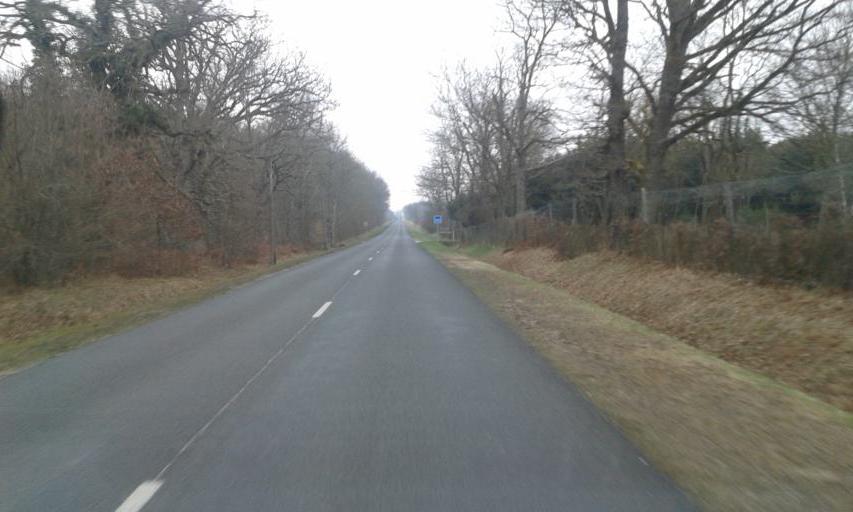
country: FR
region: Centre
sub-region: Departement du Loir-et-Cher
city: Saint-Laurent-Nouan
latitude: 47.6830
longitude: 1.6679
